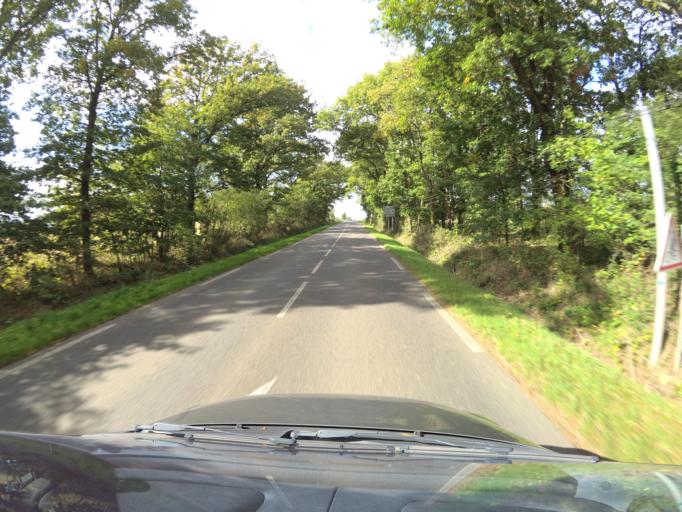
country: FR
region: Pays de la Loire
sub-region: Departement de la Loire-Atlantique
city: Plesse
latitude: 47.5137
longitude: -1.8840
